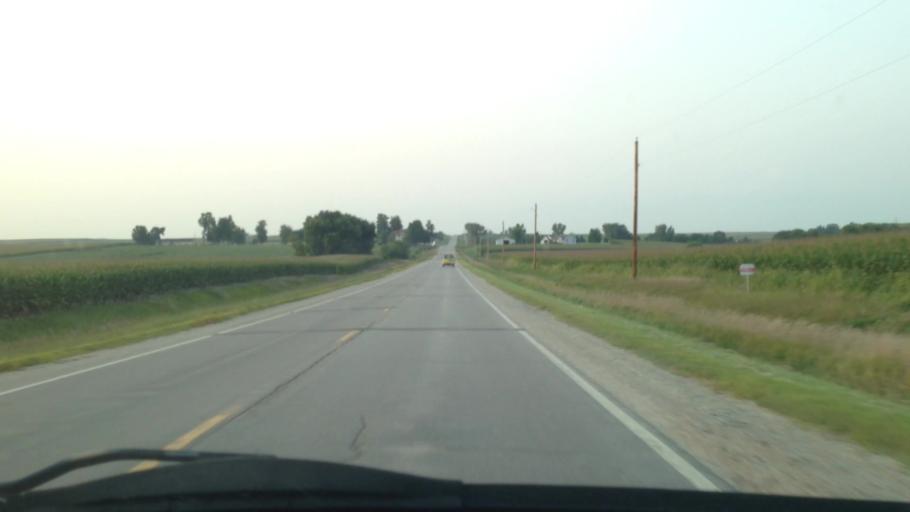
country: US
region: Iowa
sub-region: Benton County
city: Atkins
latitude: 42.0008
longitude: -91.8735
